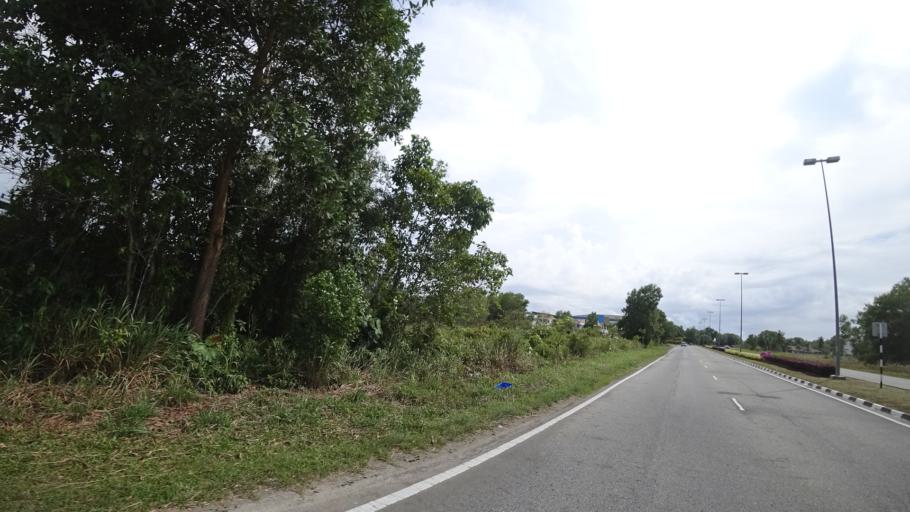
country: BN
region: Tutong
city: Tutong
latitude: 4.8144
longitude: 114.6577
